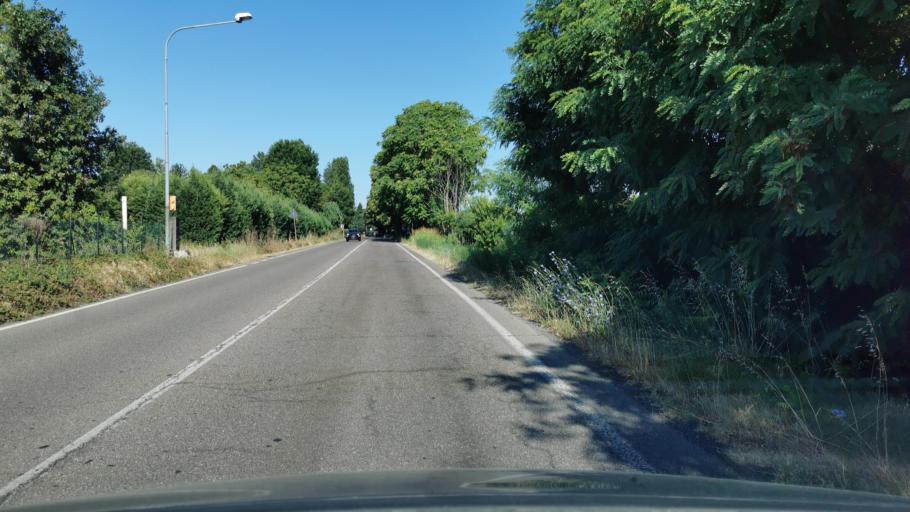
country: IT
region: Emilia-Romagna
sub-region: Provincia di Modena
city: Modena
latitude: 44.6193
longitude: 10.8999
